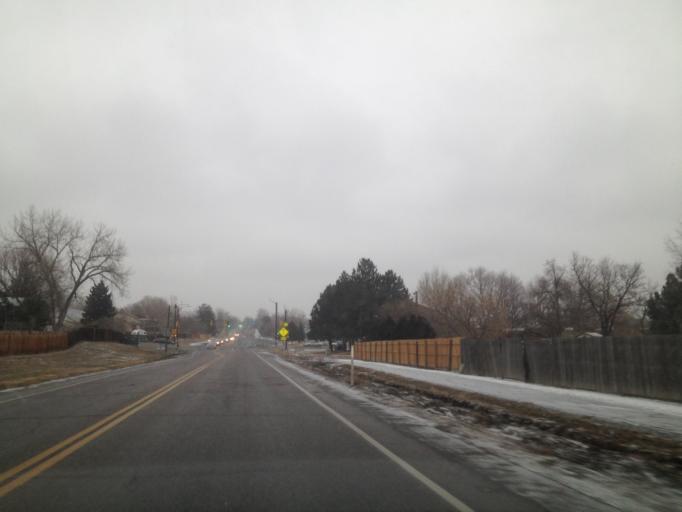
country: US
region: Colorado
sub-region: Jefferson County
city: Arvada
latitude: 39.8271
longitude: -105.1305
